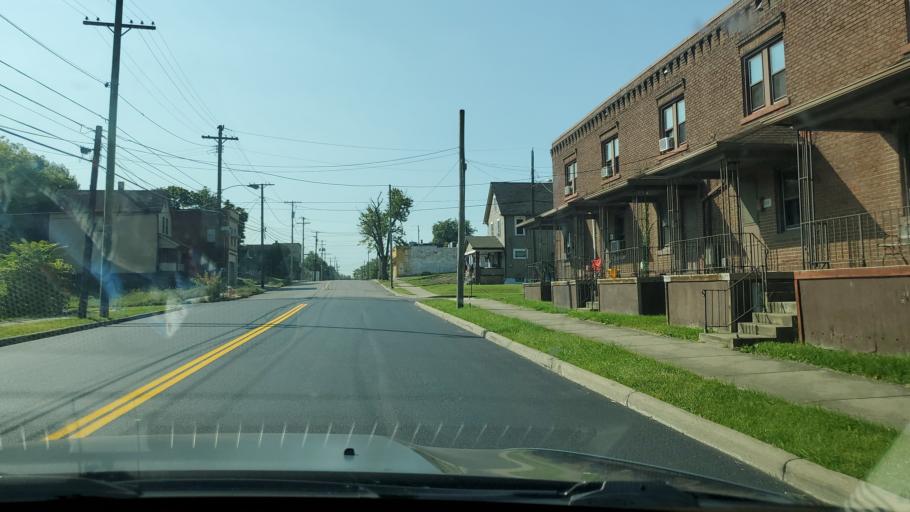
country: US
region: Ohio
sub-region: Mahoning County
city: Youngstown
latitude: 41.1113
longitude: -80.6828
